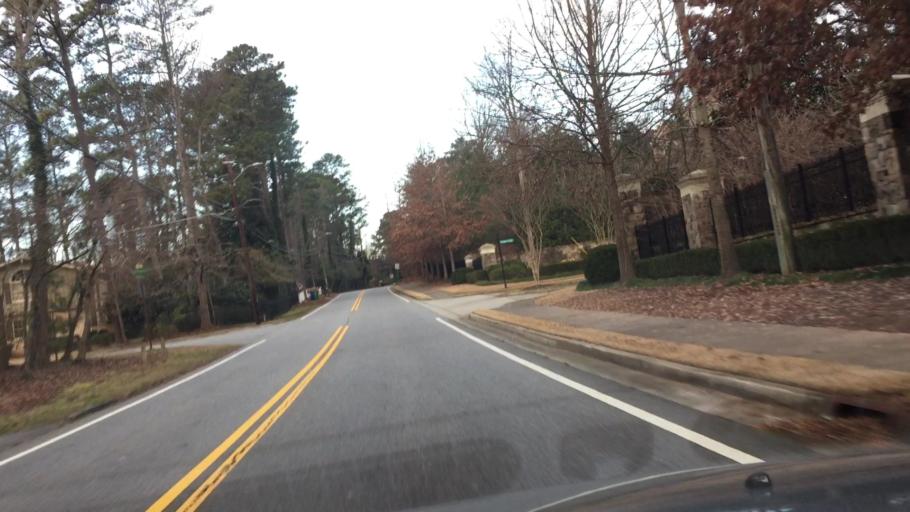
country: US
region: Georgia
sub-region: DeKalb County
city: Dunwoody
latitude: 33.9697
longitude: -84.3335
